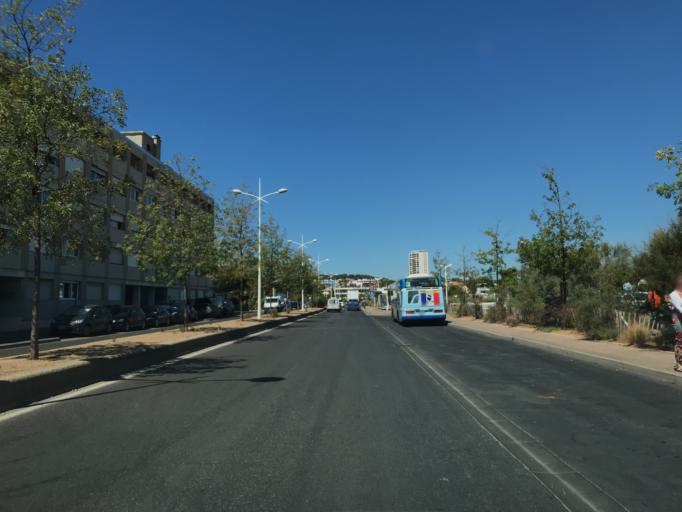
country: FR
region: Provence-Alpes-Cote d'Azur
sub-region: Departement du Var
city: La Seyne-sur-Mer
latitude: 43.0800
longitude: 5.8975
